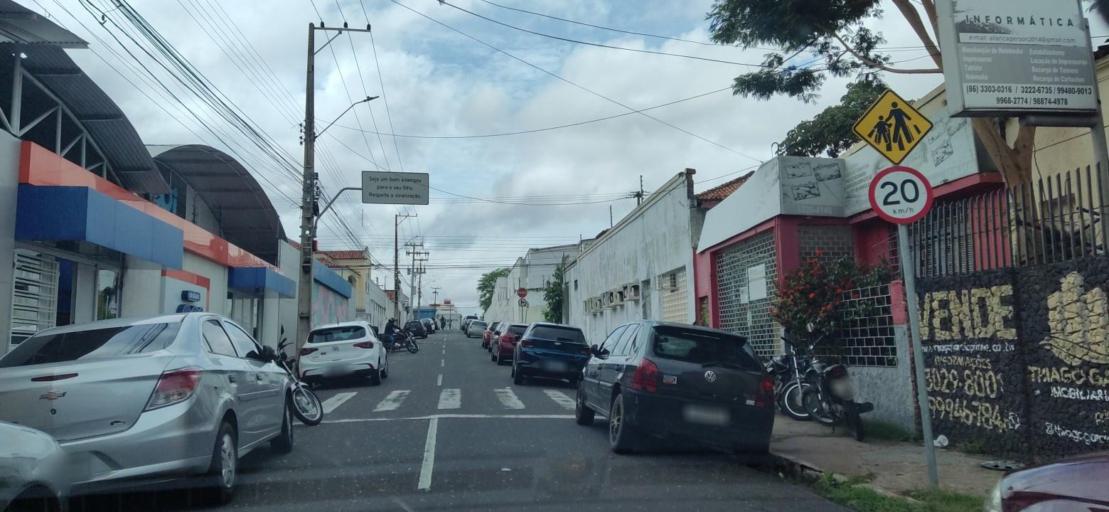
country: BR
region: Piaui
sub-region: Teresina
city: Teresina
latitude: -5.0857
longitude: -42.8104
